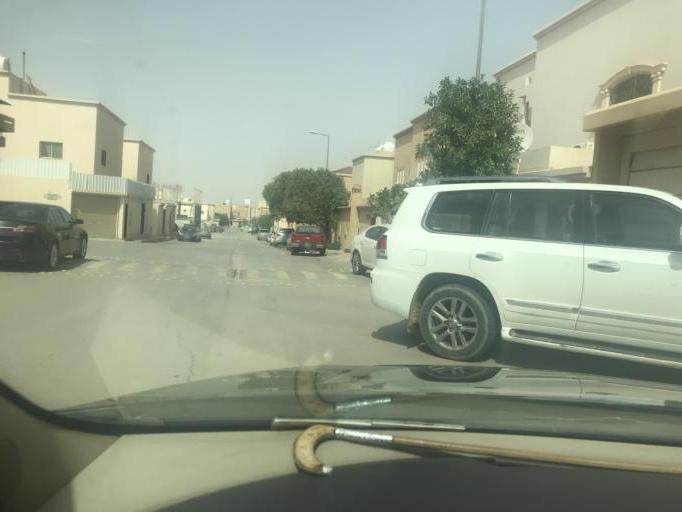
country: SA
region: Ar Riyad
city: Riyadh
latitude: 24.7612
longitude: 46.7663
